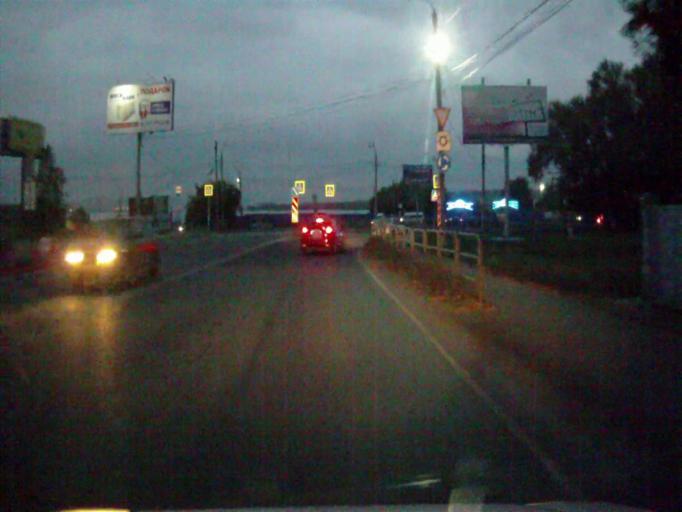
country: RU
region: Chelyabinsk
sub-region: Gorod Chelyabinsk
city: Chelyabinsk
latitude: 55.1492
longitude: 61.3029
